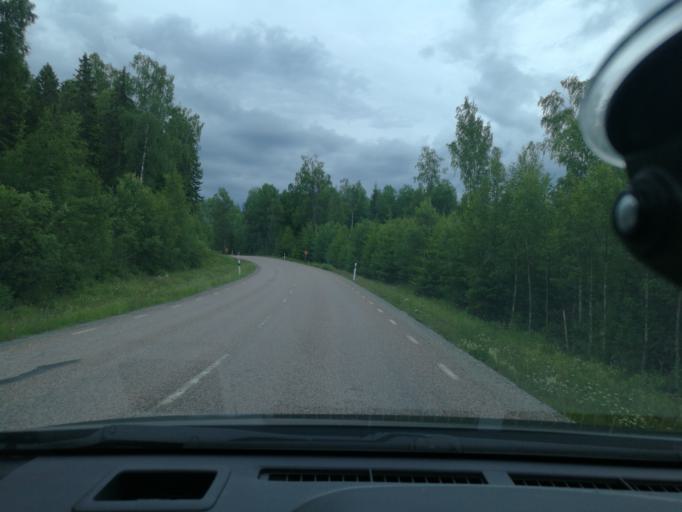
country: SE
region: Vaestmanland
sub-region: Vasteras
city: Skultuna
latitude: 59.9085
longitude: 16.4029
